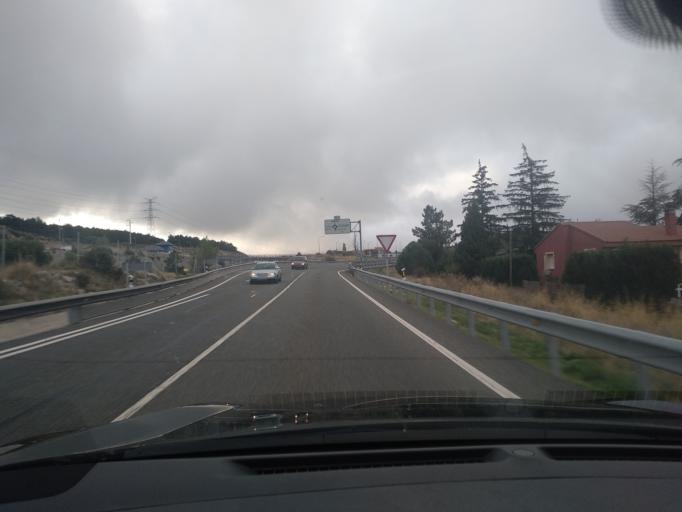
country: ES
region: Castille and Leon
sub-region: Provincia de Segovia
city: Otero de Herreros
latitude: 40.7801
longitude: -4.2094
